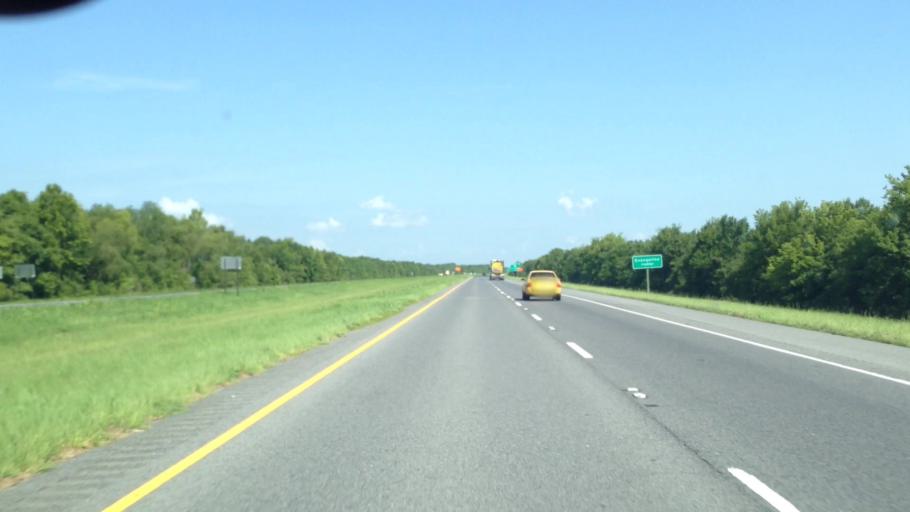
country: US
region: Louisiana
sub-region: Evangeline Parish
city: Ville Platte
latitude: 30.7634
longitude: -92.1708
